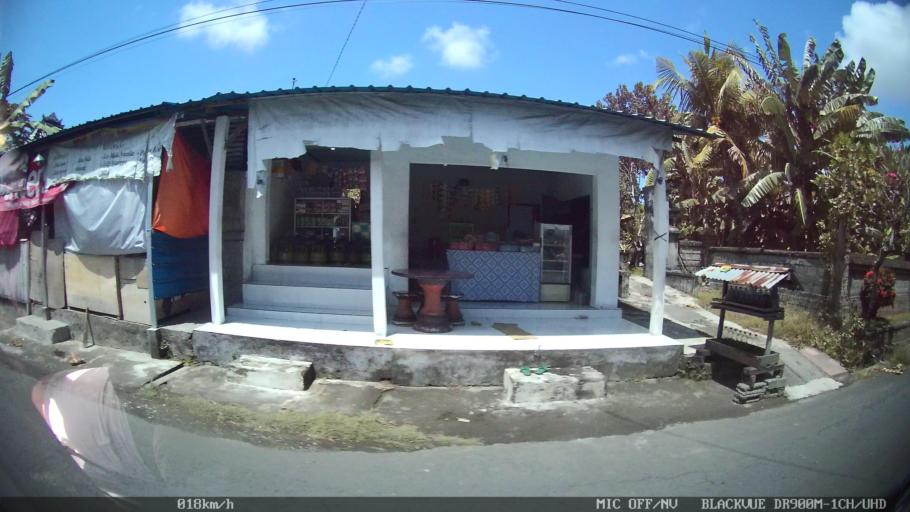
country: ID
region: Bali
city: Banjar Paangkelod
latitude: -8.6122
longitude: 115.2560
